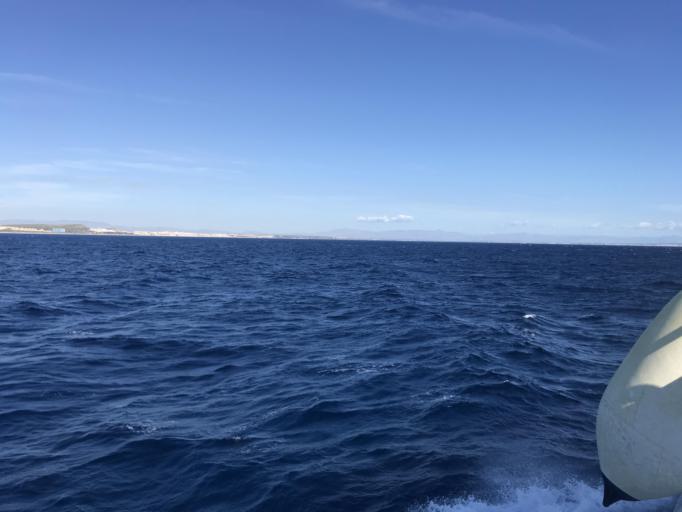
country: ES
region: Valencia
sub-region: Provincia de Alicante
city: Guardamar del Segura
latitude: 38.0296
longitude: -0.6157
